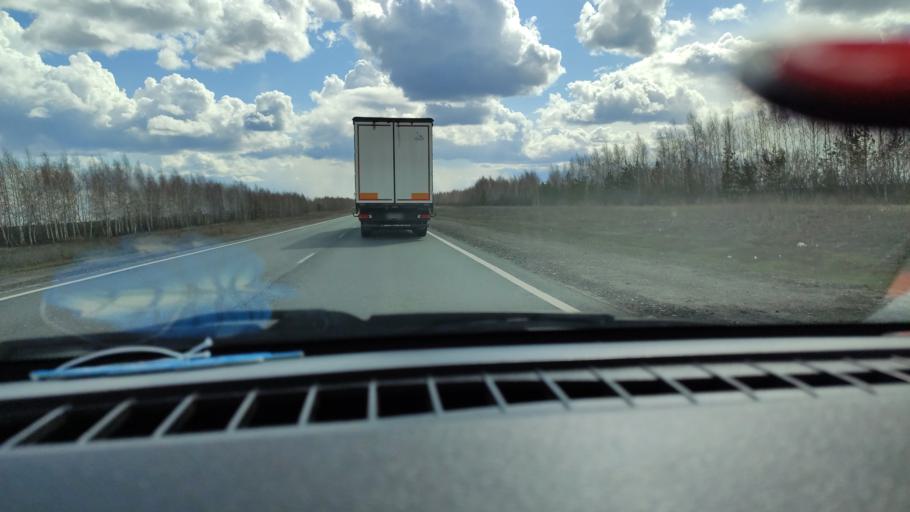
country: RU
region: Saratov
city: Dukhovnitskoye
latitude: 52.8189
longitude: 48.2331
